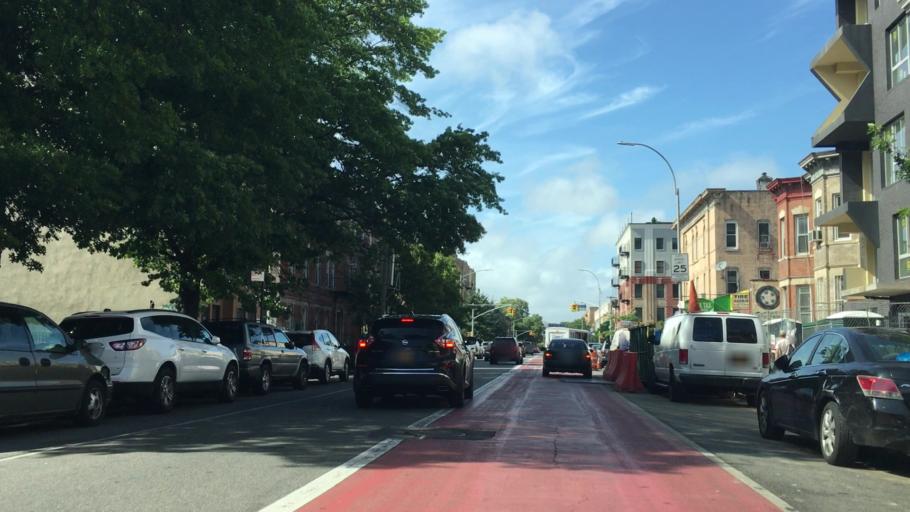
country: US
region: New York
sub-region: Kings County
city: Brooklyn
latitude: 40.6531
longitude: -73.9527
